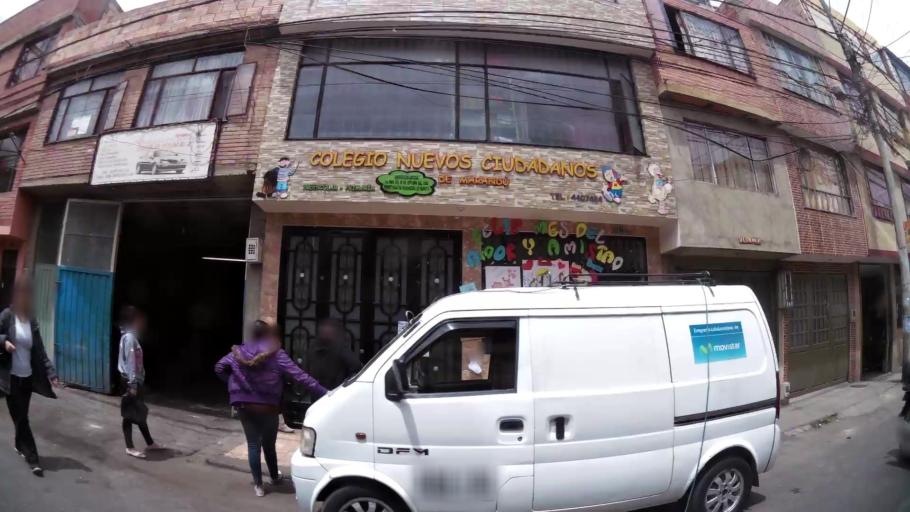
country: CO
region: Cundinamarca
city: Funza
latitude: 4.7078
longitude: -74.1306
